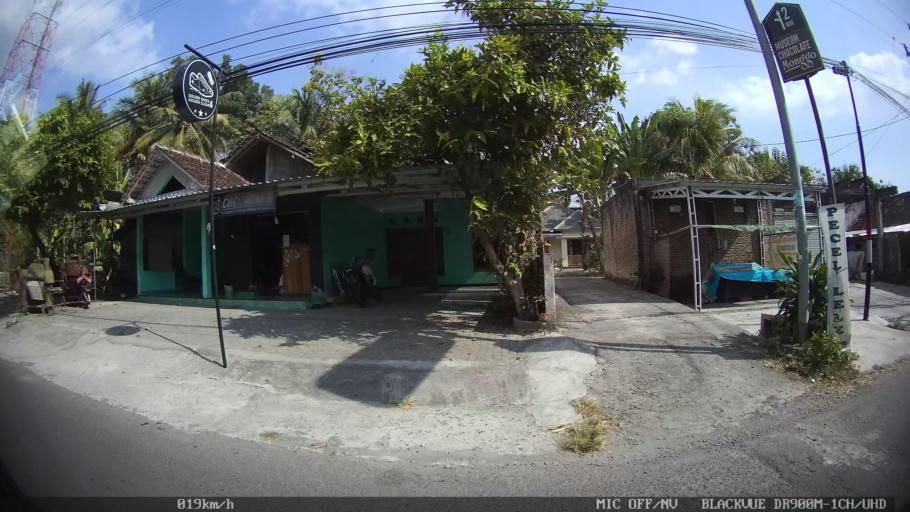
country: ID
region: Daerah Istimewa Yogyakarta
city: Kasihan
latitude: -7.8423
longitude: 110.3044
